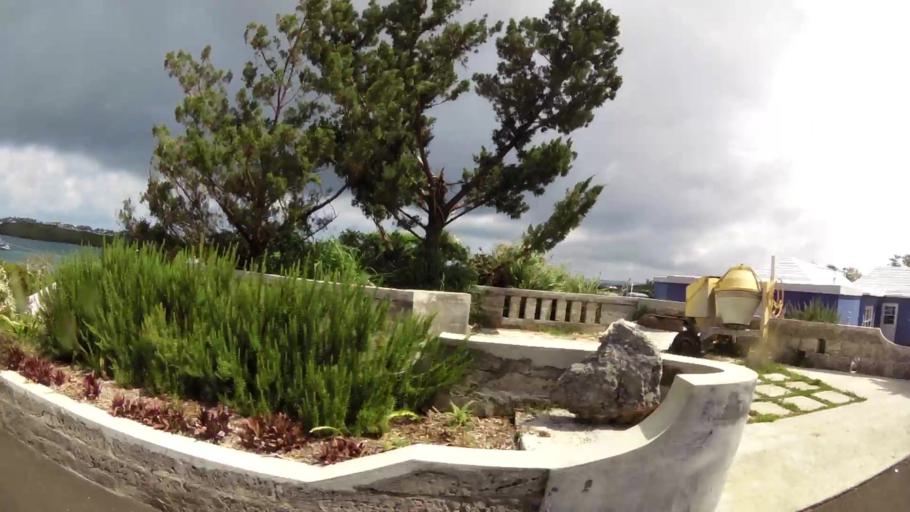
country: BM
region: Saint George
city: Saint George
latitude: 32.3668
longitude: -64.6546
